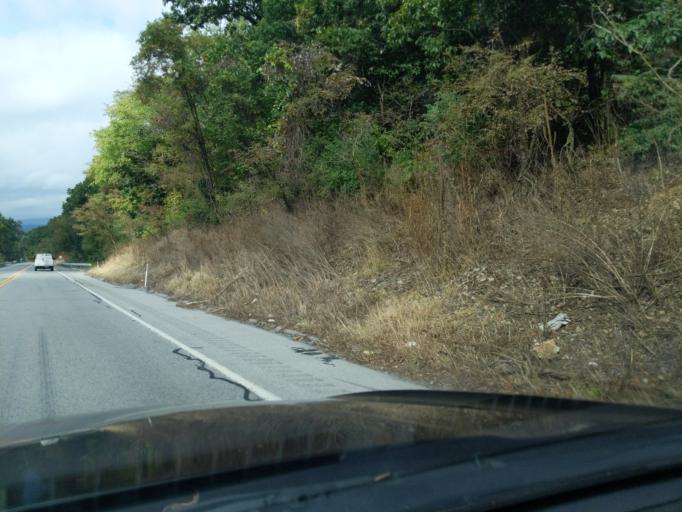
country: US
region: Pennsylvania
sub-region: Blair County
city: Hollidaysburg
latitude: 40.4041
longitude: -78.4066
